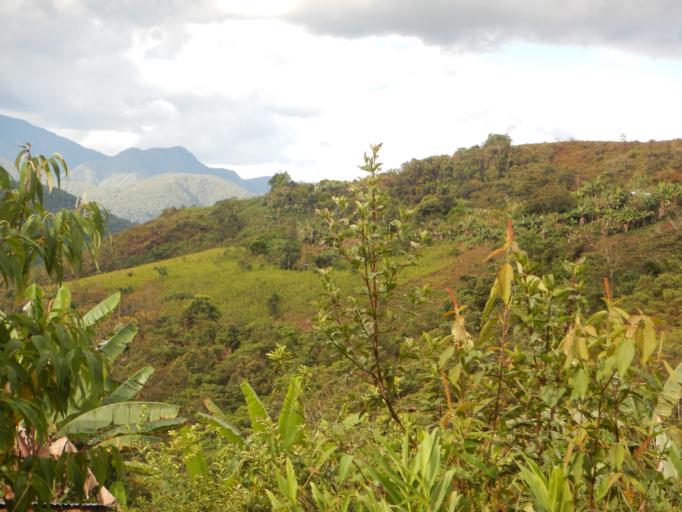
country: BO
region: La Paz
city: Coroico
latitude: -16.1290
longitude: -67.7519
